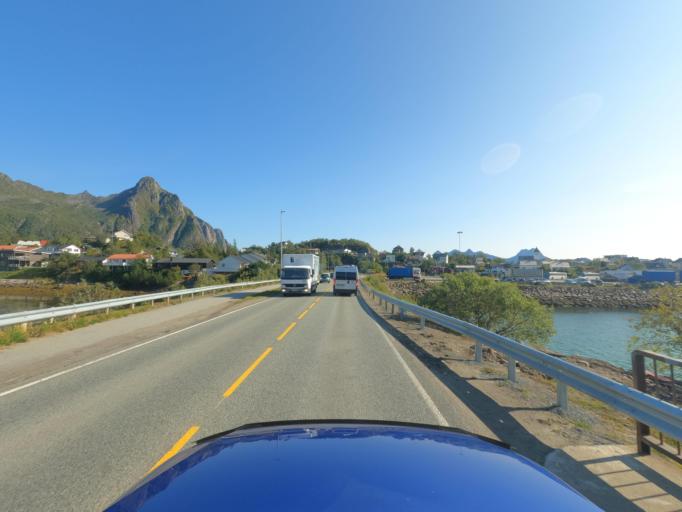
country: NO
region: Nordland
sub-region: Vagan
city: Svolvaer
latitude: 68.2362
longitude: 14.5500
